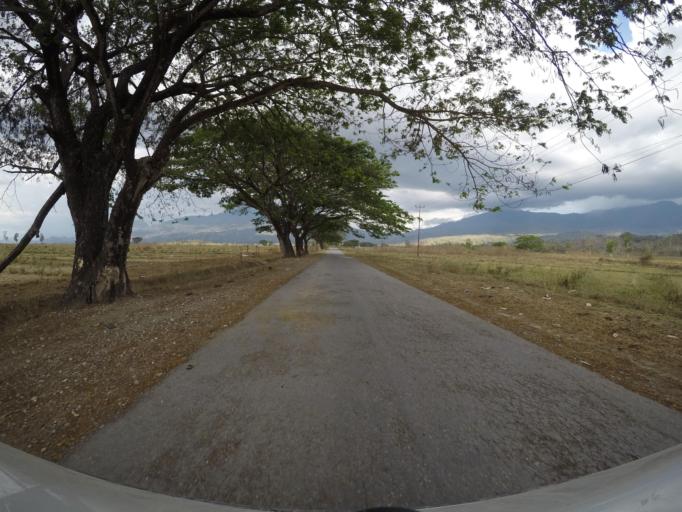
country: TL
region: Bobonaro
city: Maliana
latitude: -8.9912
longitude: 125.1783
